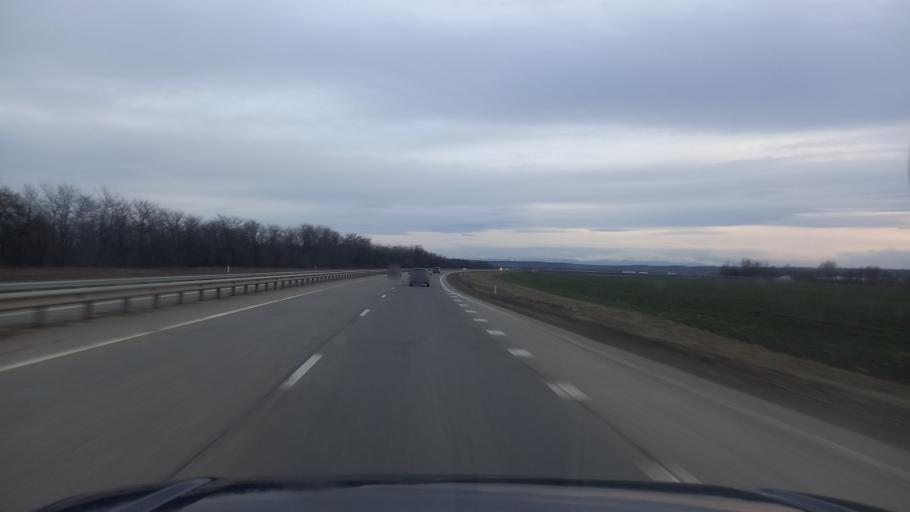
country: RU
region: Adygeya
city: Khanskaya
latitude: 44.6760
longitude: 39.9923
